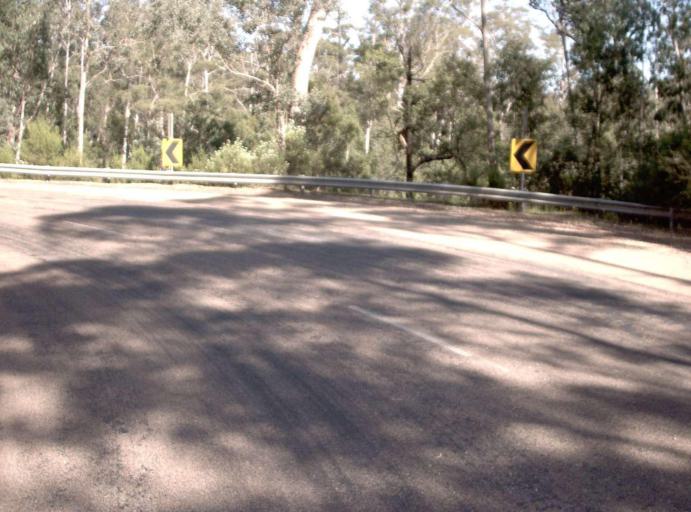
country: AU
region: Victoria
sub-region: East Gippsland
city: Lakes Entrance
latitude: -37.5118
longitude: 148.5479
